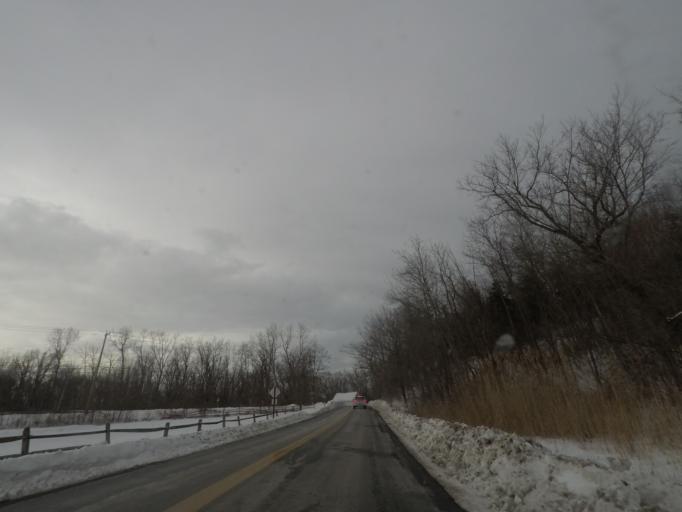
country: US
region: New York
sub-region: Rensselaer County
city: Castleton-on-Hudson
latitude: 42.5177
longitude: -73.7589
